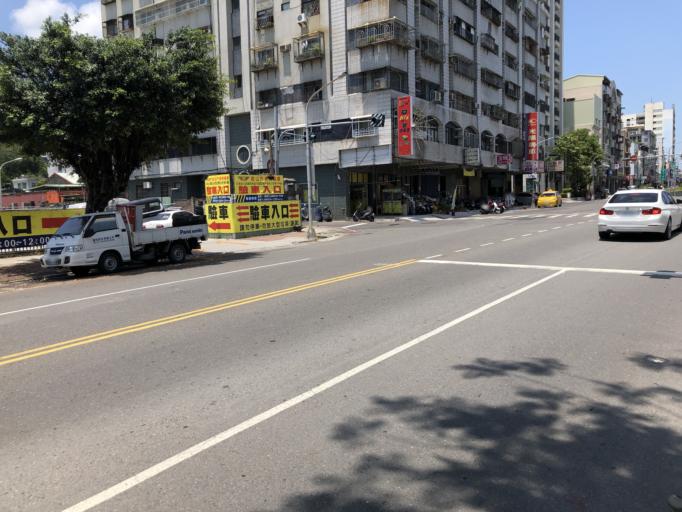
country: TW
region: Kaohsiung
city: Kaohsiung
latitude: 22.6283
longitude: 120.2797
